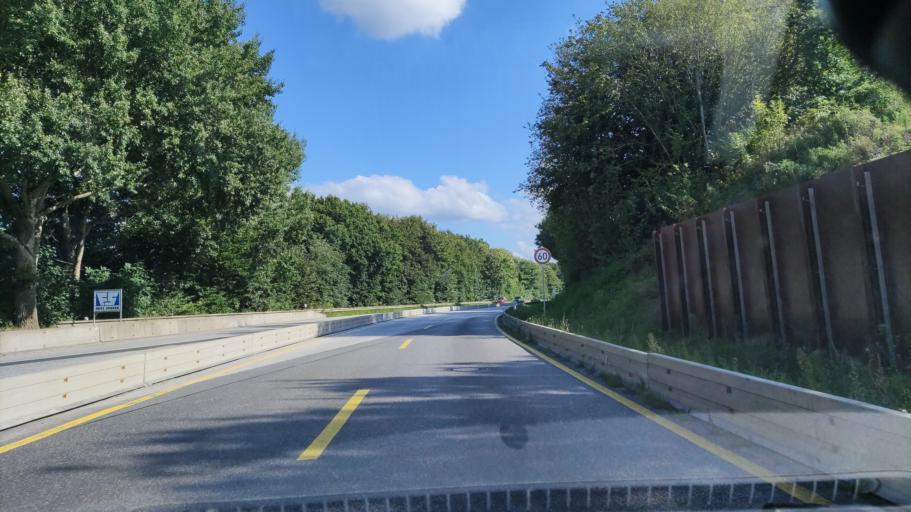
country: DE
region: Schleswig-Holstein
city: Rendsburg
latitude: 54.2998
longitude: 9.6492
